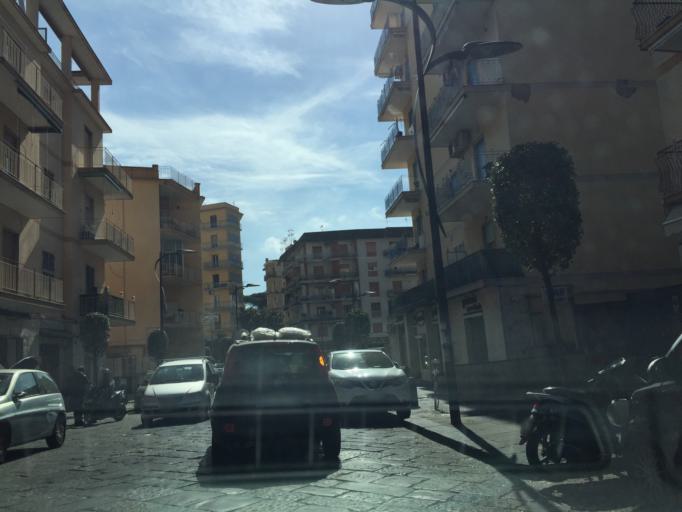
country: IT
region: Campania
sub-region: Provincia di Napoli
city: Ercolano
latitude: 40.8092
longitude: 14.3536
